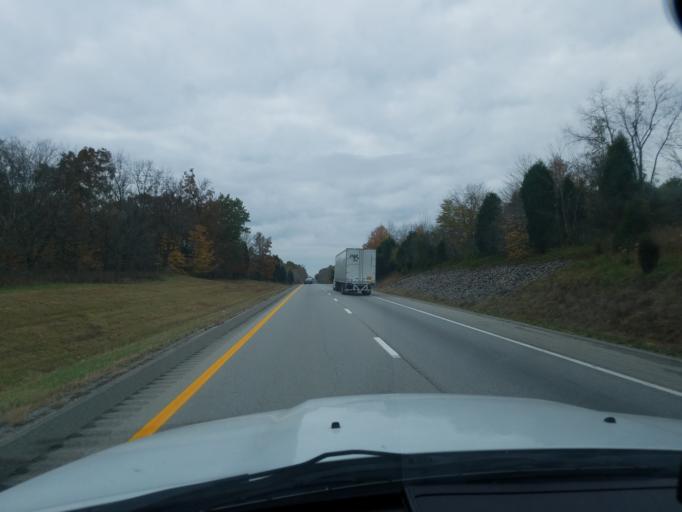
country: US
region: Kentucky
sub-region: Oldham County
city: La Grange
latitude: 38.4219
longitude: -85.3331
